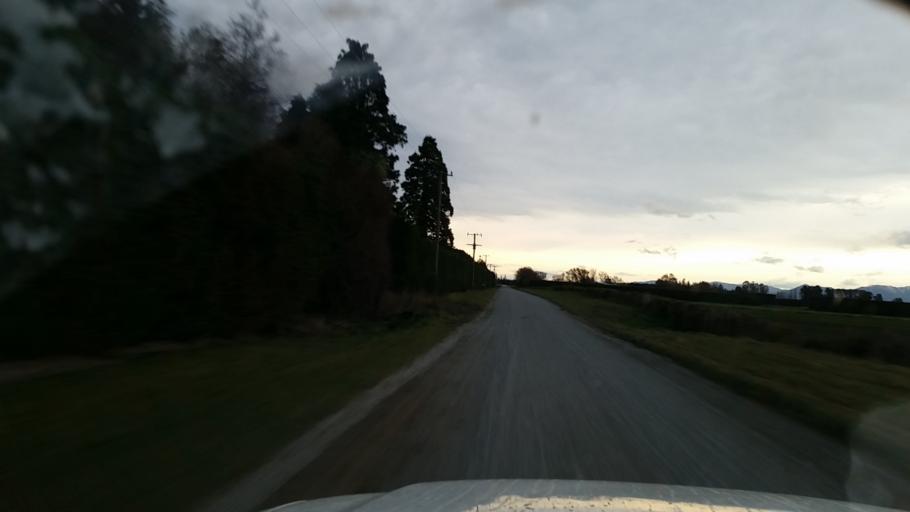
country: NZ
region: Canterbury
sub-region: Ashburton District
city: Ashburton
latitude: -43.8320
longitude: 171.6254
